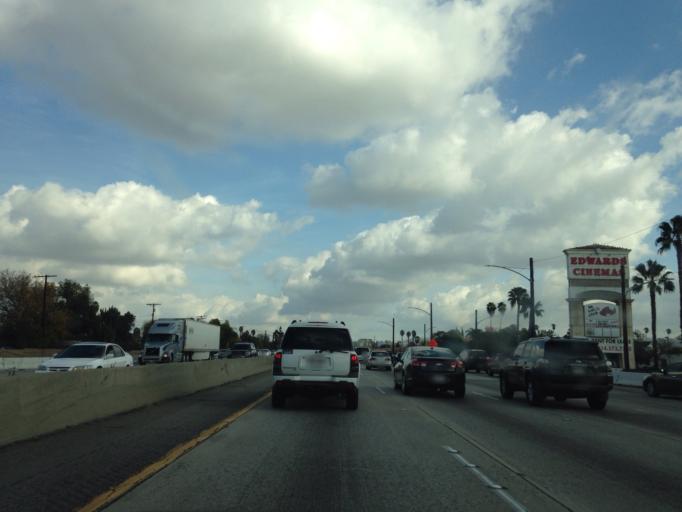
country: US
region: California
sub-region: Los Angeles County
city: West Covina
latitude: 34.0722
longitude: -117.9224
